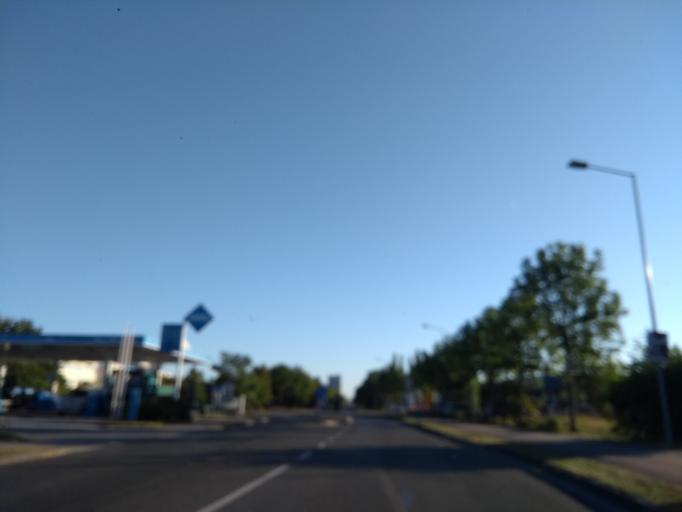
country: DE
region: Brandenburg
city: Lubbenau
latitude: 51.8528
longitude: 13.9495
